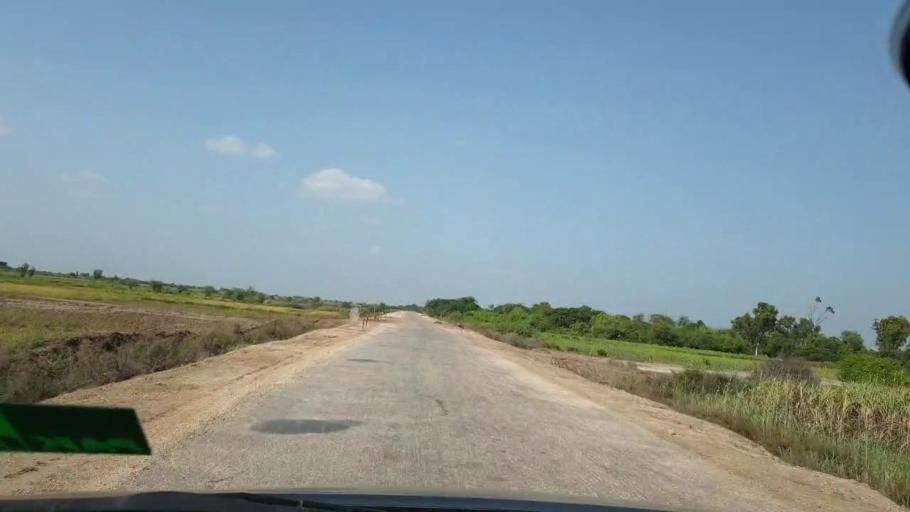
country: PK
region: Sindh
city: Tando Bago
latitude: 24.6896
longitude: 69.1886
